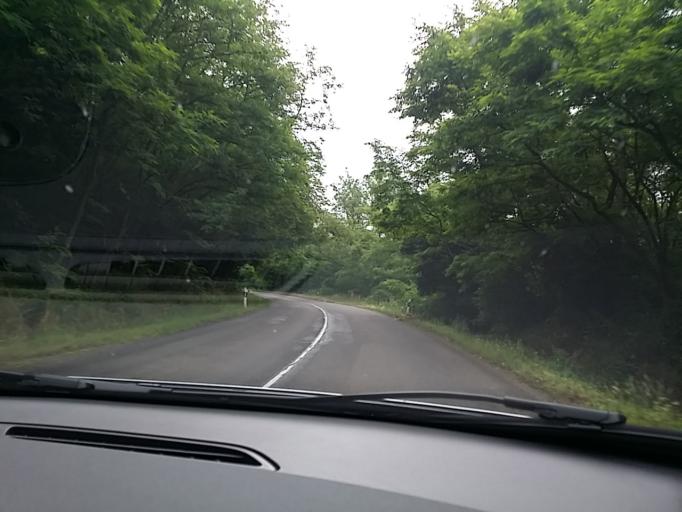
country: HU
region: Nograd
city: Matranovak
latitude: 48.0070
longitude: 19.9966
